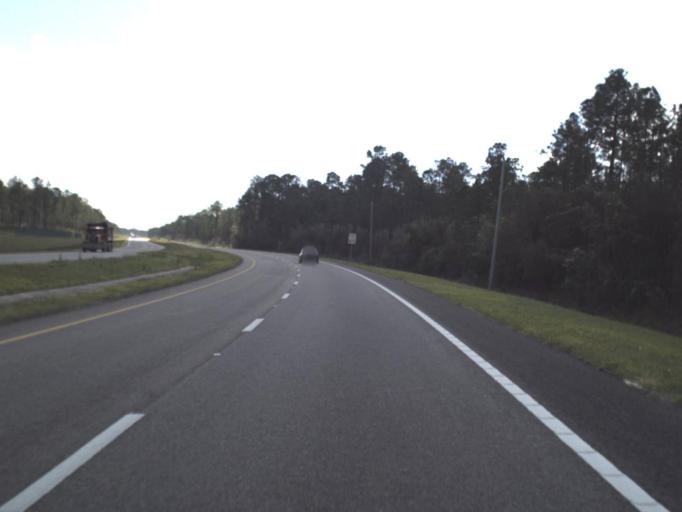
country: US
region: Florida
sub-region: Bay County
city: Laguna Beach
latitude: 30.3903
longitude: -85.8728
